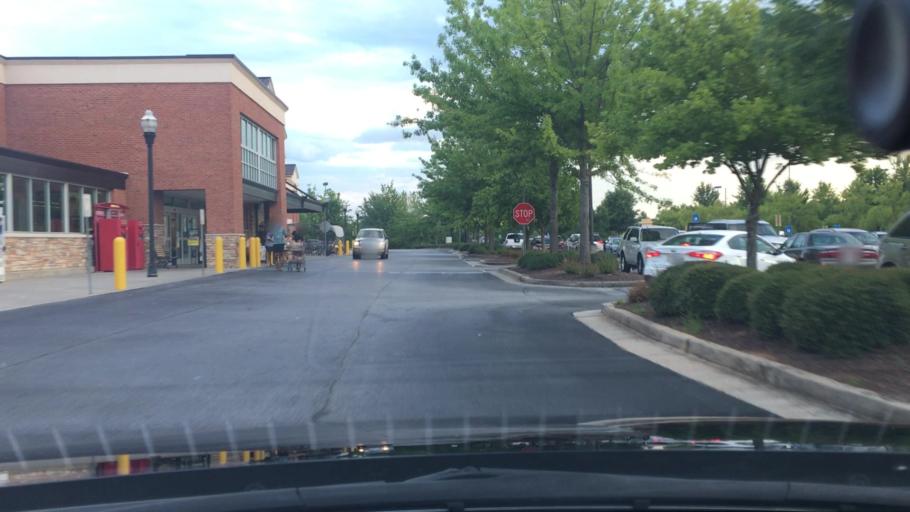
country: US
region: Georgia
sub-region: Coweta County
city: East Newnan
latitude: 33.3776
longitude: -84.7522
